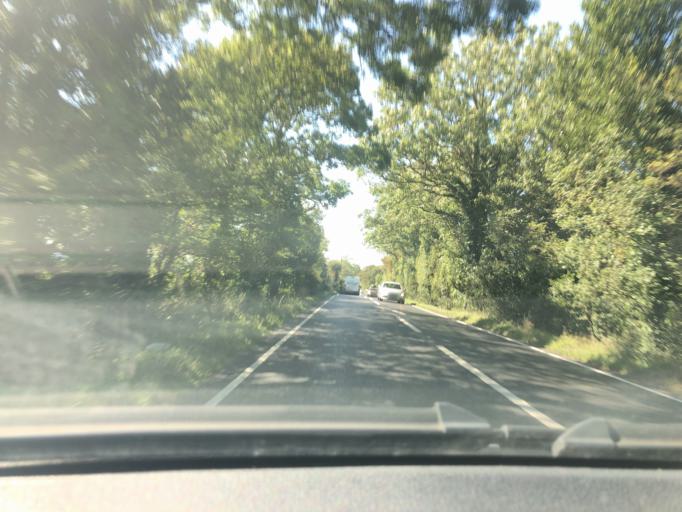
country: GB
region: England
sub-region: Somerset
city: Woolavington
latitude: 51.1452
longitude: -2.8936
